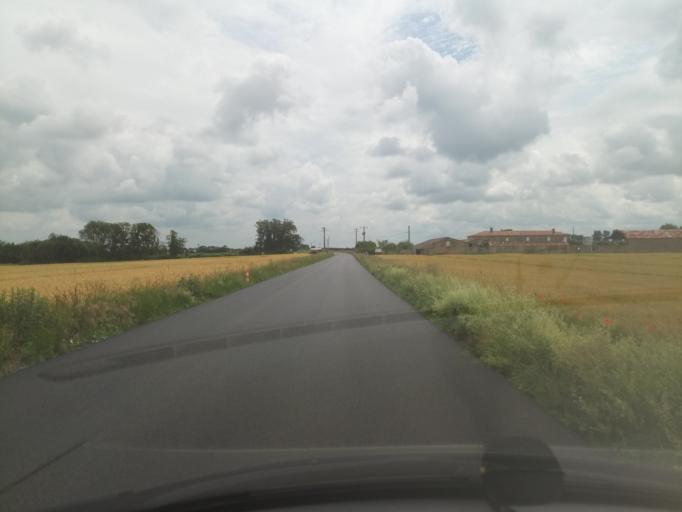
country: FR
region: Poitou-Charentes
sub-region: Departement de la Charente-Maritime
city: Saint-Jean-de-Liversay
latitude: 46.2713
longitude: -0.8964
